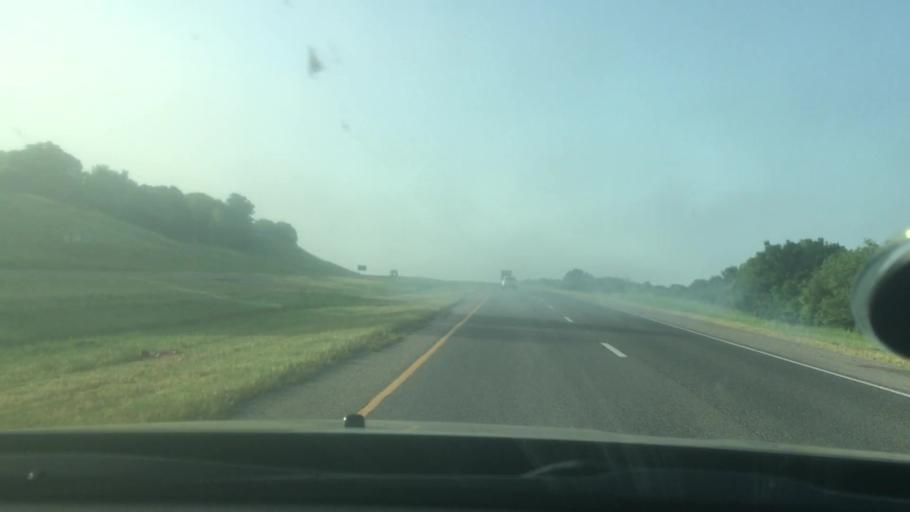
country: US
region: Oklahoma
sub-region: Pontotoc County
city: Ada
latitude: 34.7331
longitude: -96.6414
